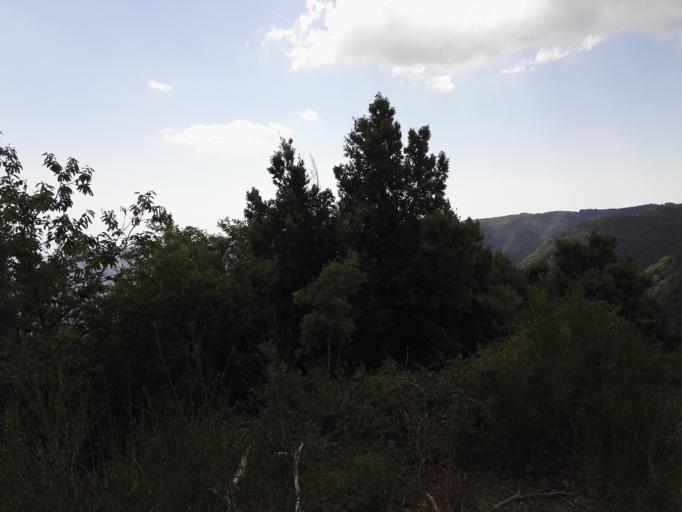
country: IT
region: Calabria
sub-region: Provincia di Reggio Calabria
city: Bivongi
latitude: 38.5080
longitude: 16.3961
